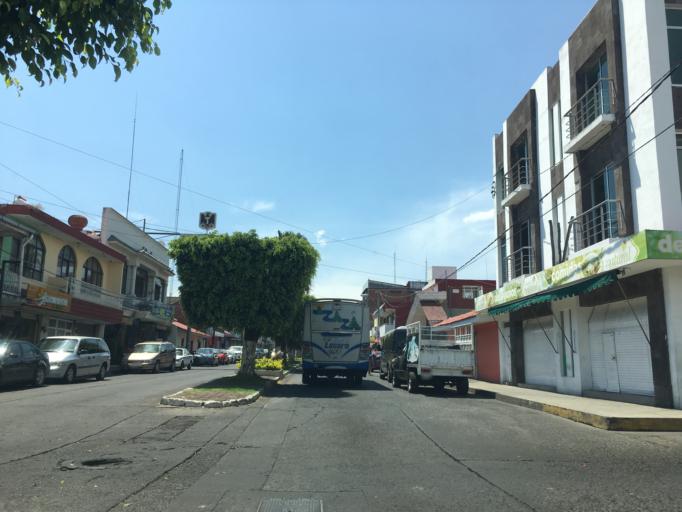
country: MX
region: Michoacan
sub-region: Uruapan
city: Uruapan
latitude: 19.4157
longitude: -102.0544
